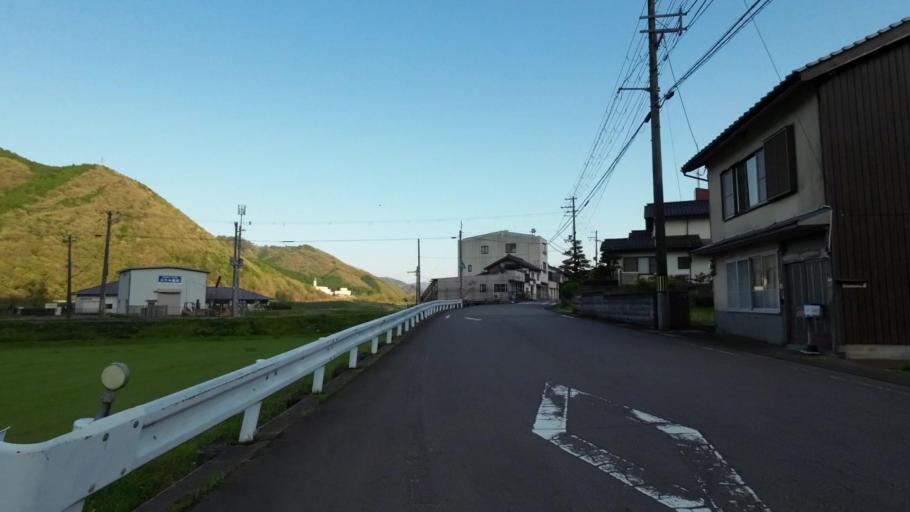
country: JP
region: Hyogo
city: Toyooka
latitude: 35.3723
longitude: 134.8113
